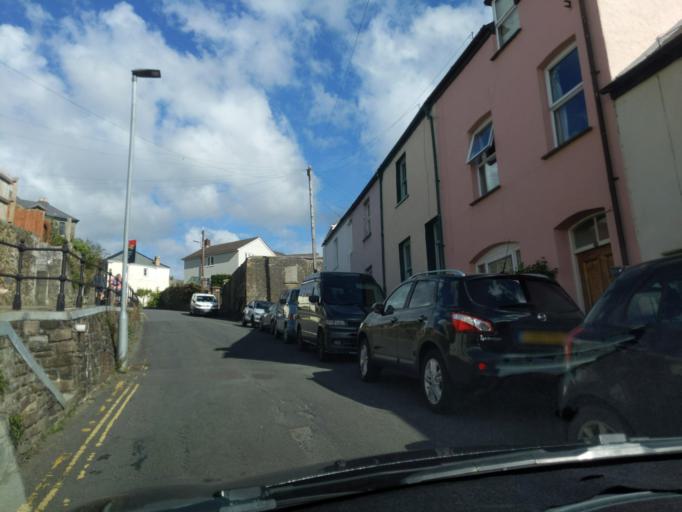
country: GB
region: England
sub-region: Devon
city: Great Torrington
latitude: 50.9504
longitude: -4.1481
